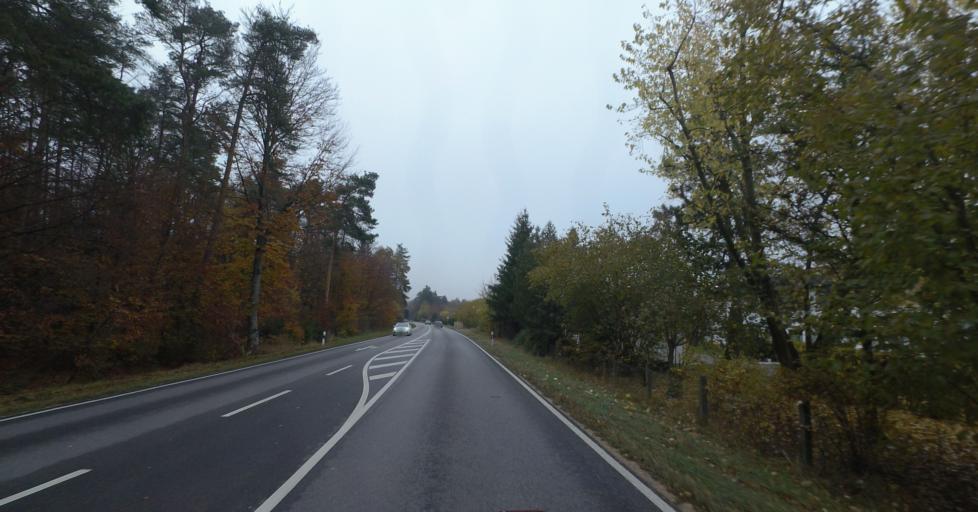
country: DE
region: Bavaria
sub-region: Upper Bavaria
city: Garching an der Alz
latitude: 48.1392
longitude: 12.5983
